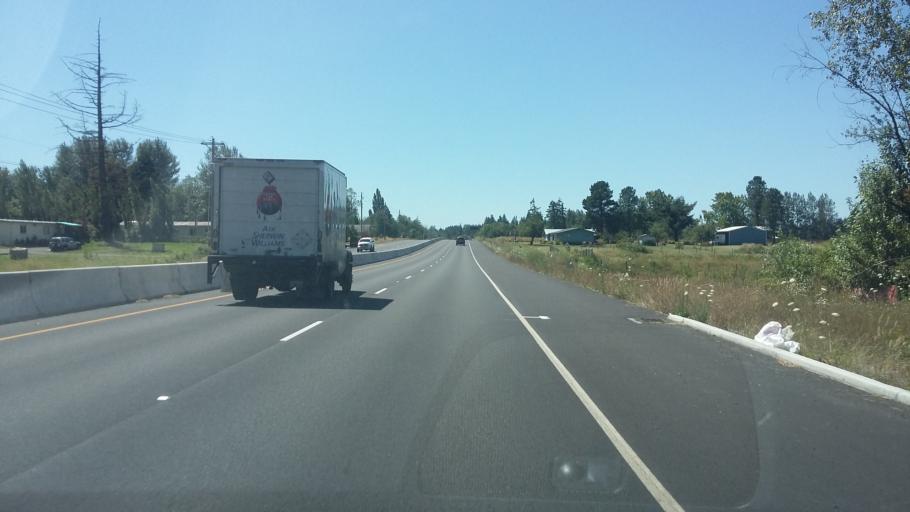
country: US
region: Washington
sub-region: Clark County
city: Mount Vista
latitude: 45.7798
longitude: -122.6507
